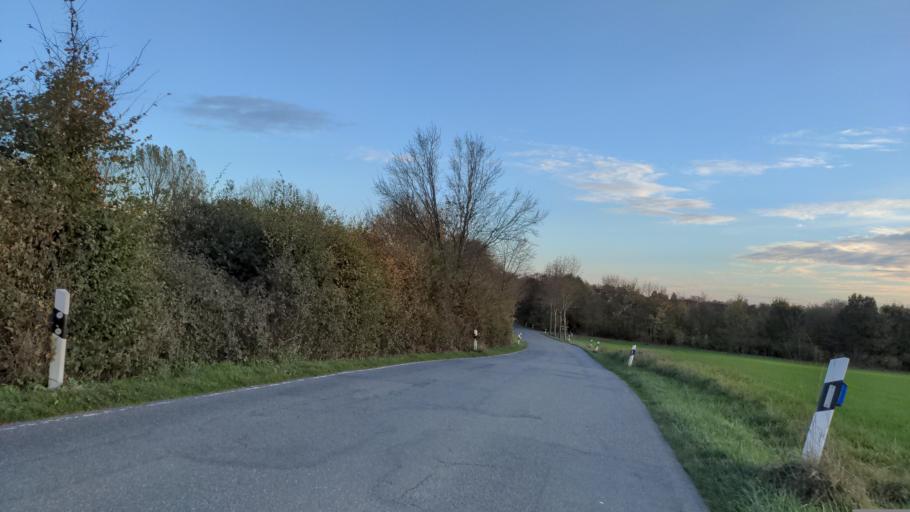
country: DE
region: Schleswig-Holstein
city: Reinfeld
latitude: 53.8390
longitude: 10.4756
